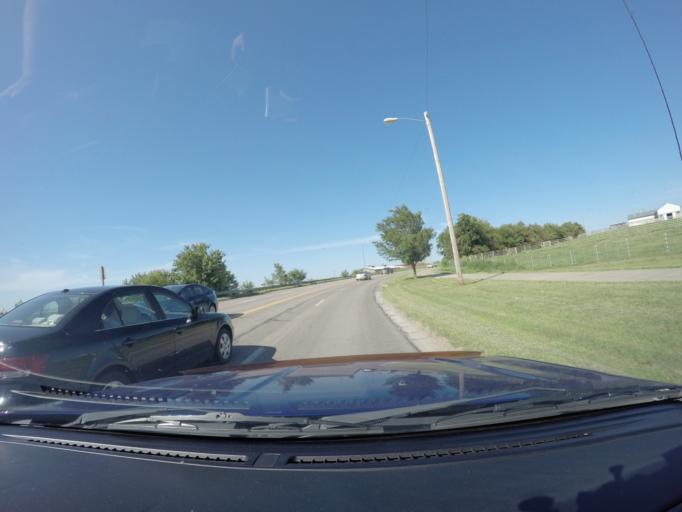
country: US
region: Kansas
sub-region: Riley County
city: Manhattan
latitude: 39.2054
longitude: -96.5821
